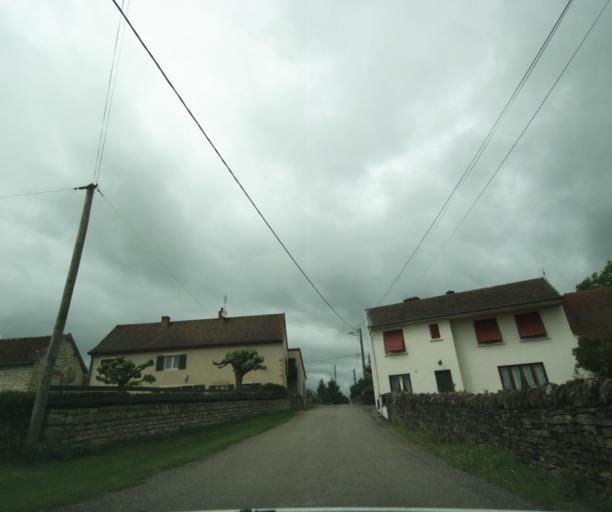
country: FR
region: Bourgogne
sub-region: Departement de Saone-et-Loire
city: Charolles
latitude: 46.4426
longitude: 4.2771
